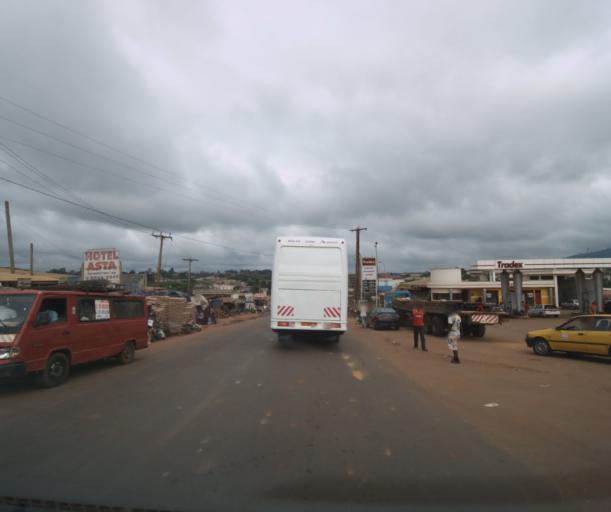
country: CM
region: Centre
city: Yaounde
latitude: 3.7950
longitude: 11.4936
